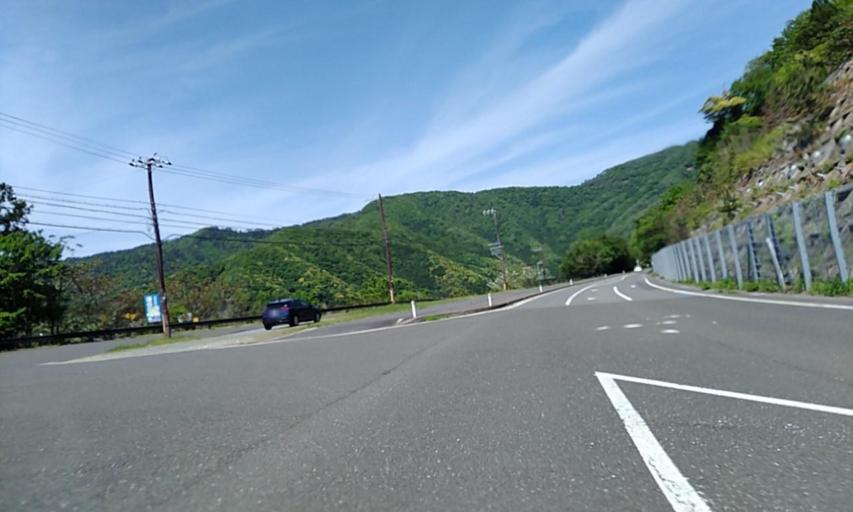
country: JP
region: Fukui
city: Obama
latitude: 35.5334
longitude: 135.8288
